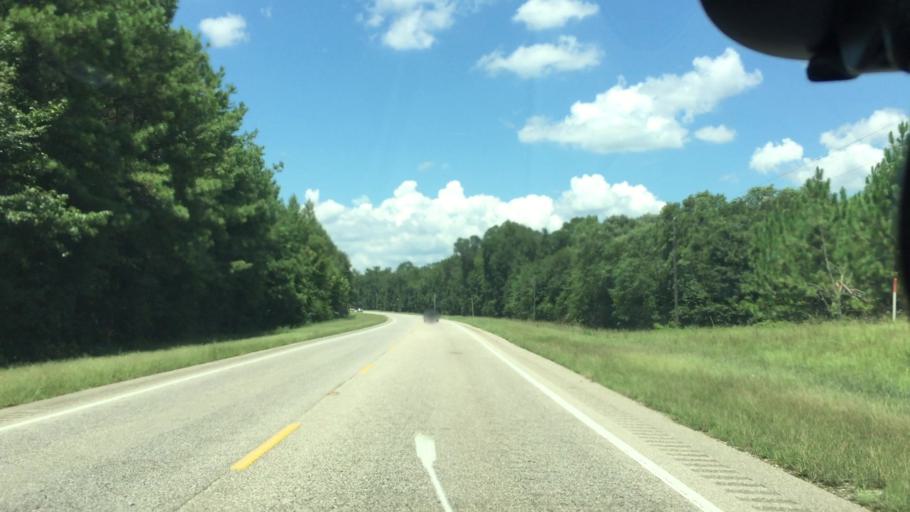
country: US
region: Alabama
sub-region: Pike County
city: Brundidge
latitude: 31.6321
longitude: -85.9455
